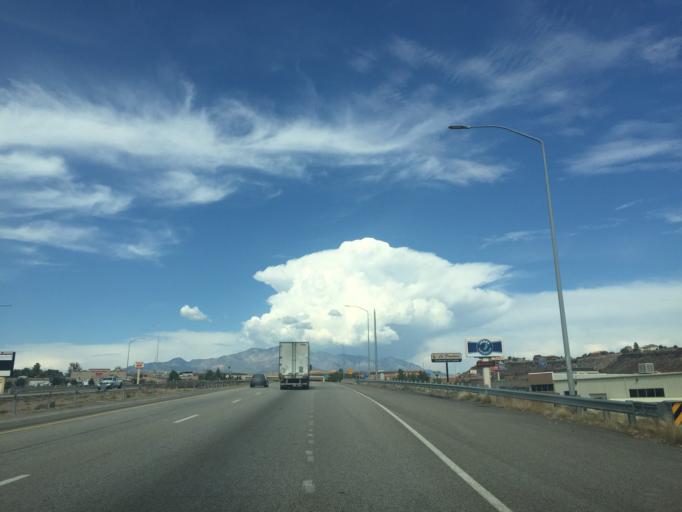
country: US
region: Utah
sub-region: Washington County
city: Saint George
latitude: 37.1053
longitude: -113.5596
